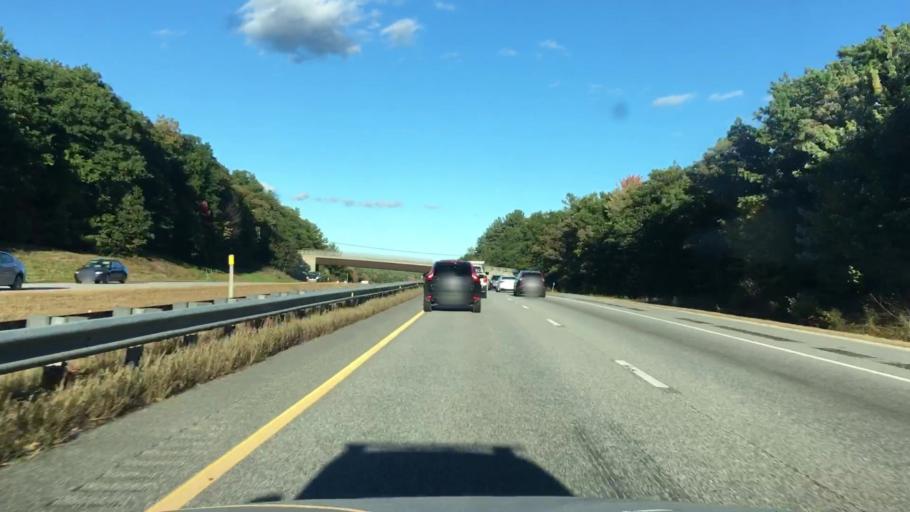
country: US
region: New Hampshire
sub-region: Rockingham County
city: Auburn
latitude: 43.0330
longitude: -71.3425
